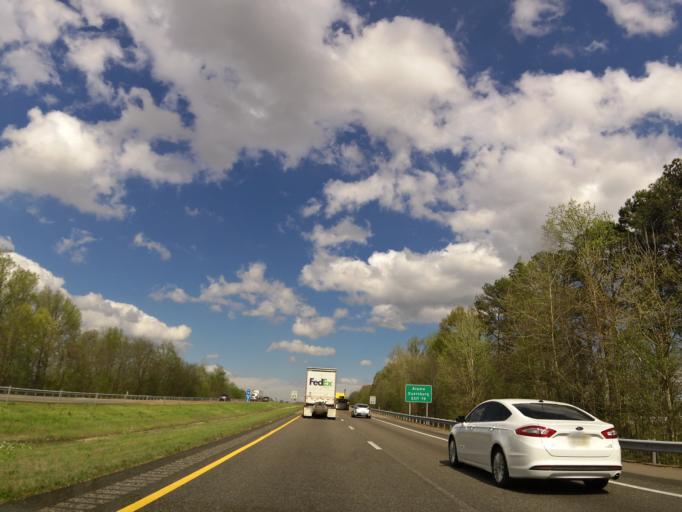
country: US
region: Tennessee
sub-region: Madison County
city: Jackson
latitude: 35.6545
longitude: -88.8803
